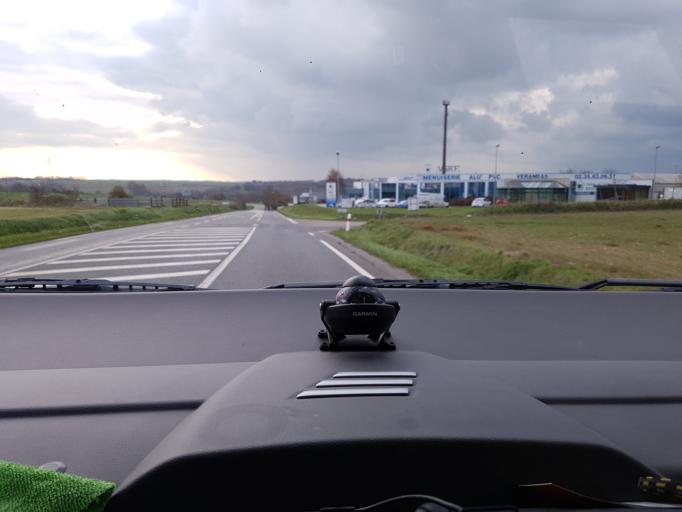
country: FR
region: Haute-Normandie
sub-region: Departement de la Seine-Maritime
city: Varengeville-sur-Mer
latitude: 49.8800
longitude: 0.9678
